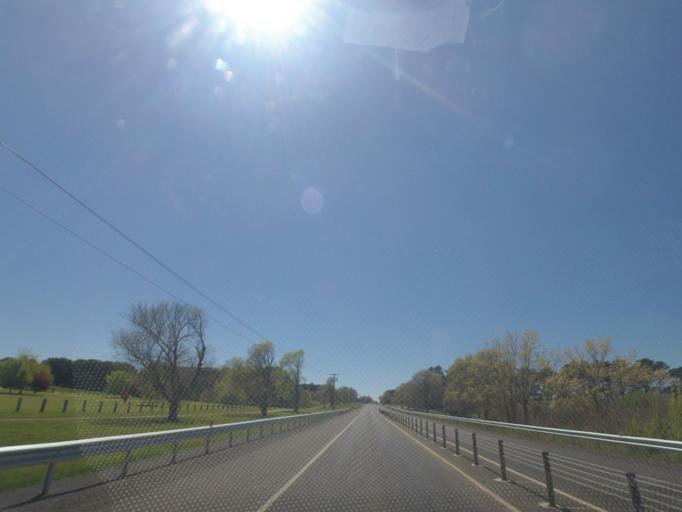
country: AU
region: Victoria
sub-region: Hume
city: Sunbury
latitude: -37.3370
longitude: 144.7414
